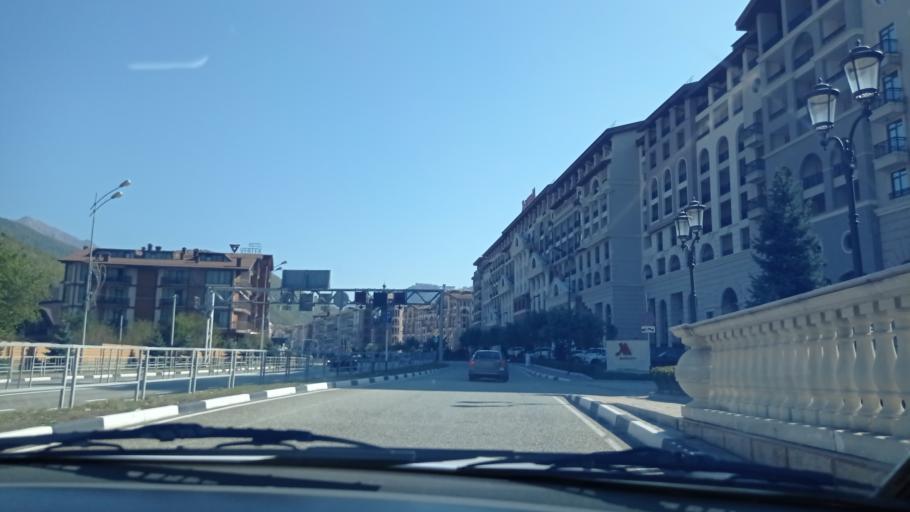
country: RU
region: Krasnodarskiy
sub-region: Sochi City
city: Krasnaya Polyana
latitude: 43.6846
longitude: 40.2554
